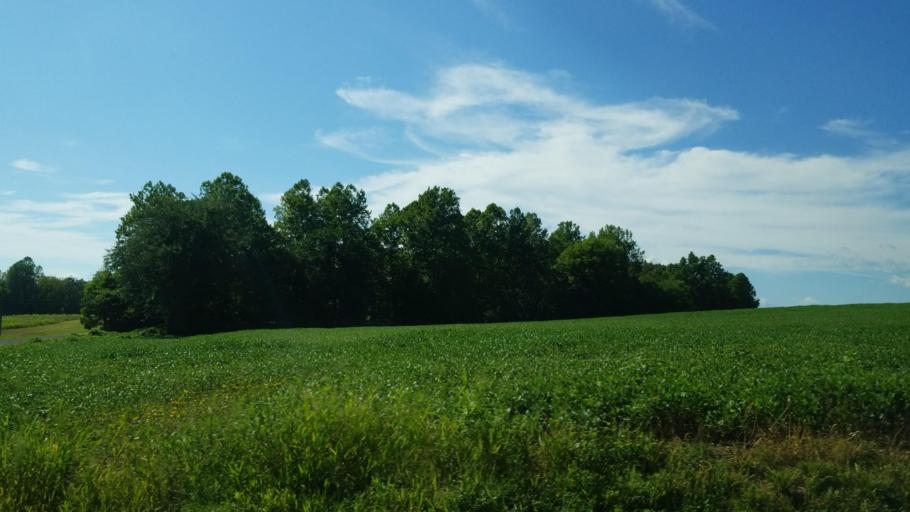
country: US
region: Illinois
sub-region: Saline County
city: Carrier Mills
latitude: 37.7979
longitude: -88.7440
